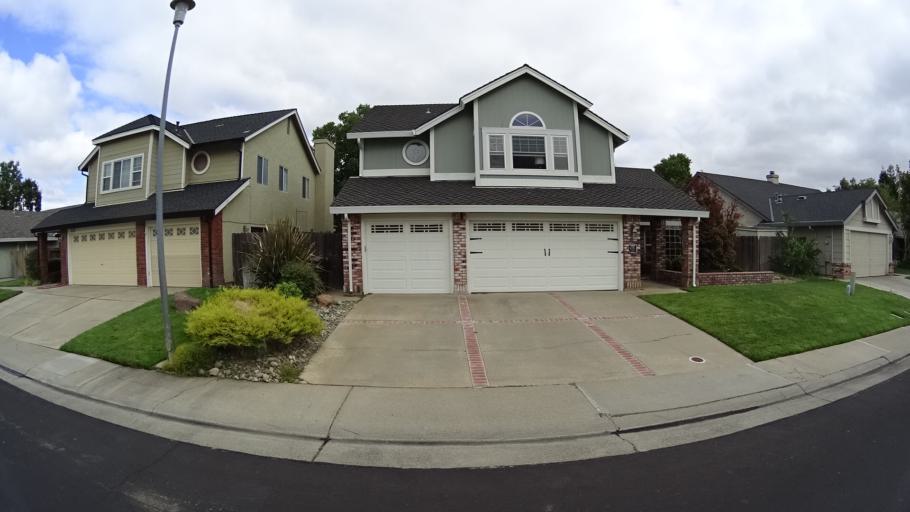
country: US
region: California
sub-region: Sacramento County
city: Laguna
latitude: 38.4116
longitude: -121.4294
